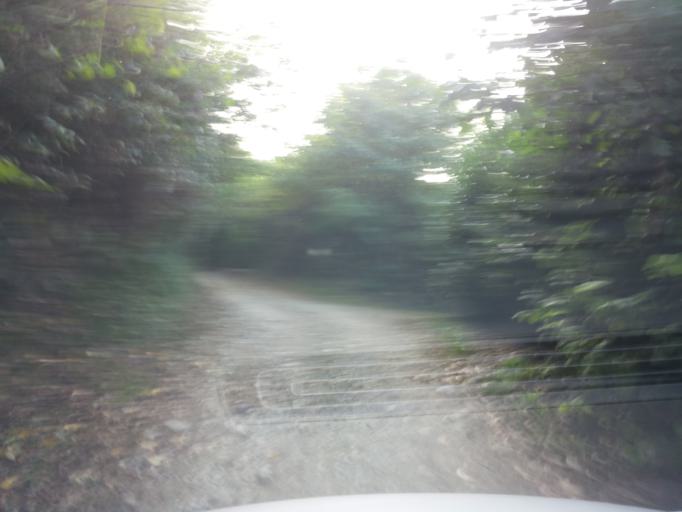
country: IT
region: Piedmont
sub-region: Provincia di Biella
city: Viverone
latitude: 45.4054
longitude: 8.0306
